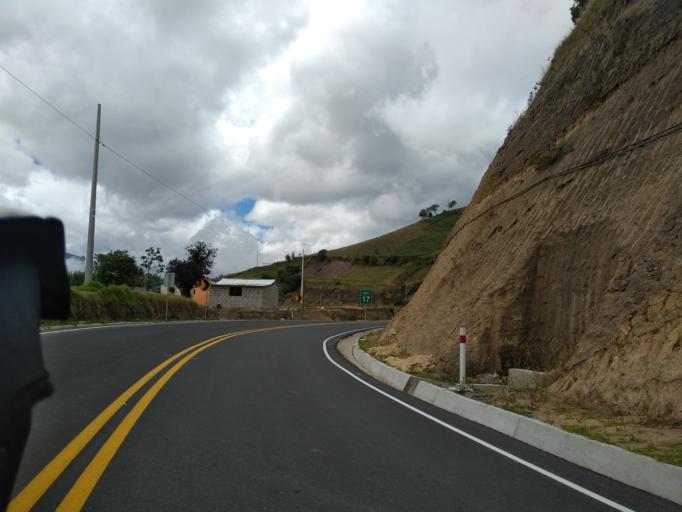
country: EC
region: Cotopaxi
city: Saquisili
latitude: -0.7665
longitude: -78.9122
